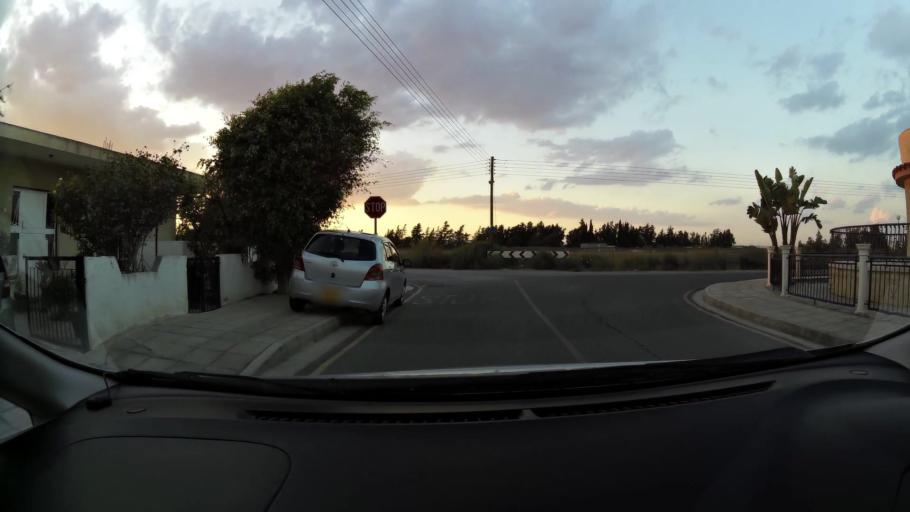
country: CY
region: Larnaka
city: Dhromolaxia
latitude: 34.8733
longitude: 33.5791
